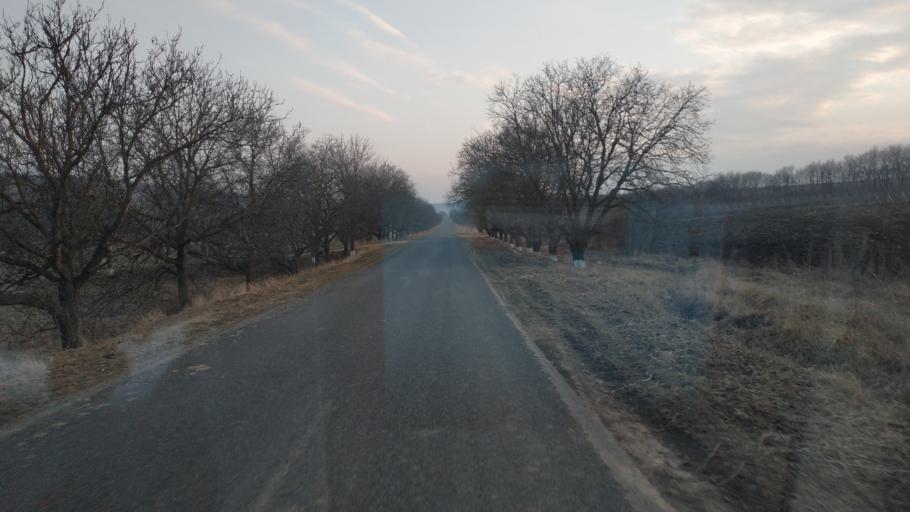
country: MD
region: Hincesti
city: Dancu
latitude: 46.6939
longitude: 28.3362
